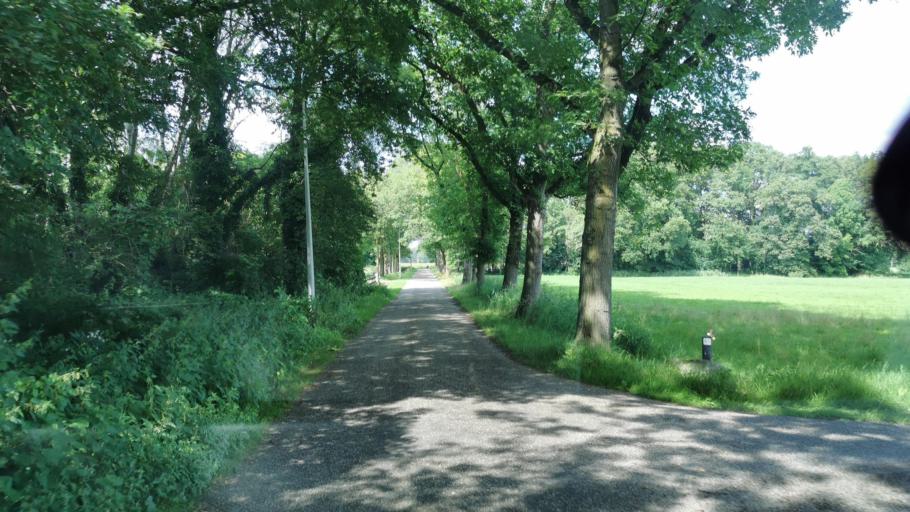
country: NL
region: Overijssel
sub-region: Gemeente Enschede
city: Enschede
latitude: 52.1692
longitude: 6.8973
